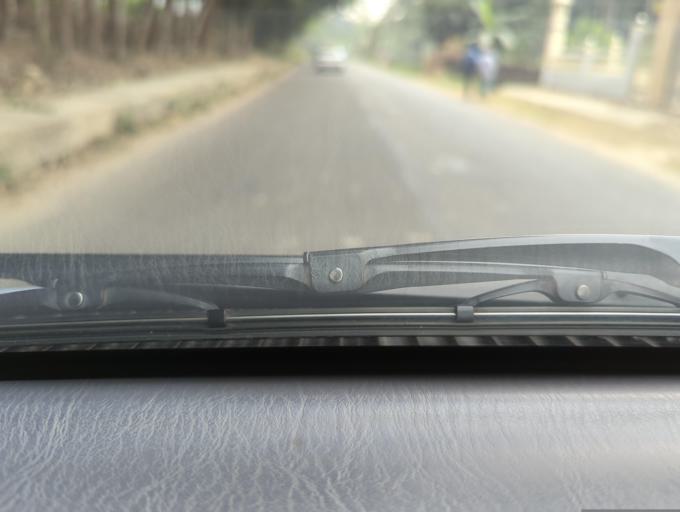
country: BD
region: Sylhet
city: Maulavi Bazar
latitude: 24.5138
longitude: 91.7259
